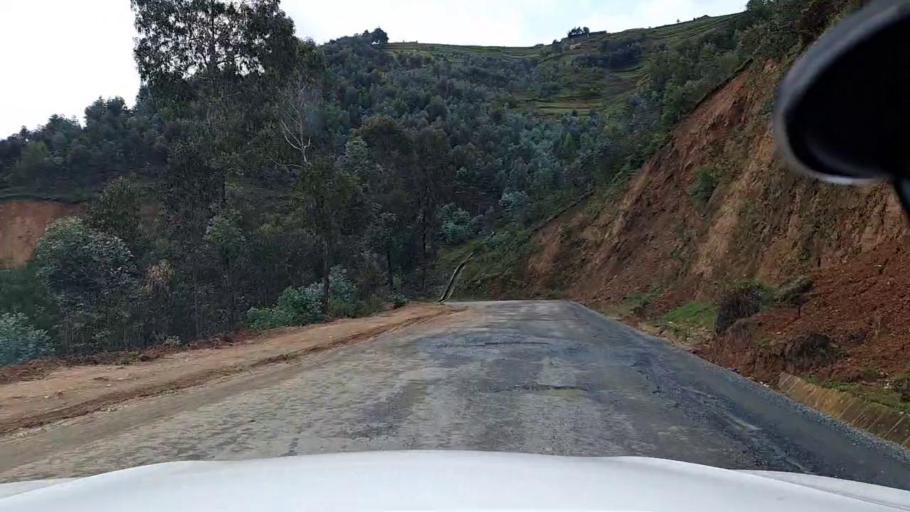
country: RW
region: Western Province
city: Kibuye
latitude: -2.0673
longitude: 29.5502
